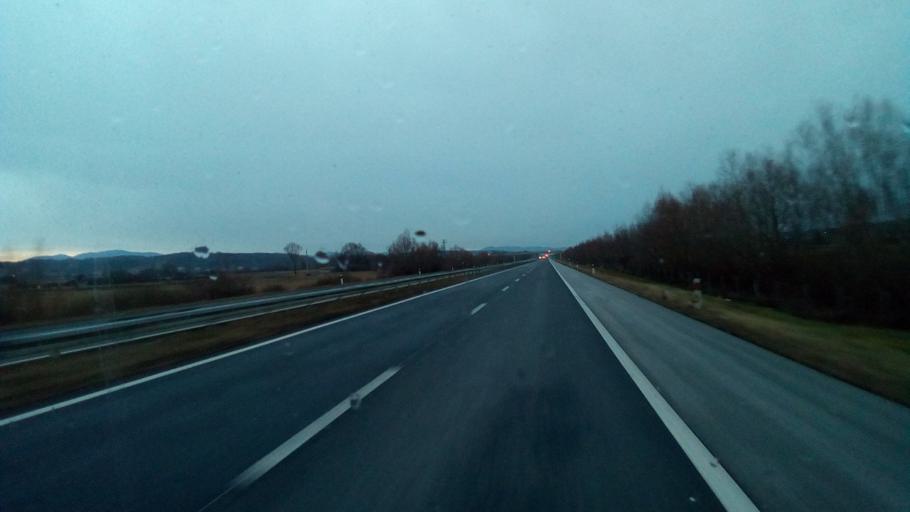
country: HR
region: Zagrebacka
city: Brckovljani
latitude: 45.9648
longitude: 16.2837
